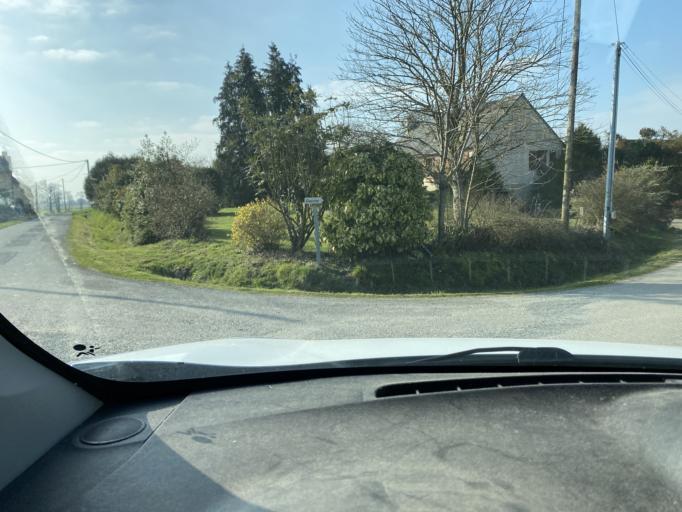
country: FR
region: Brittany
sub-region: Departement d'Ille-et-Vilaine
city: Saint-Medard-sur-Ille
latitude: 48.2512
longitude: -1.6759
